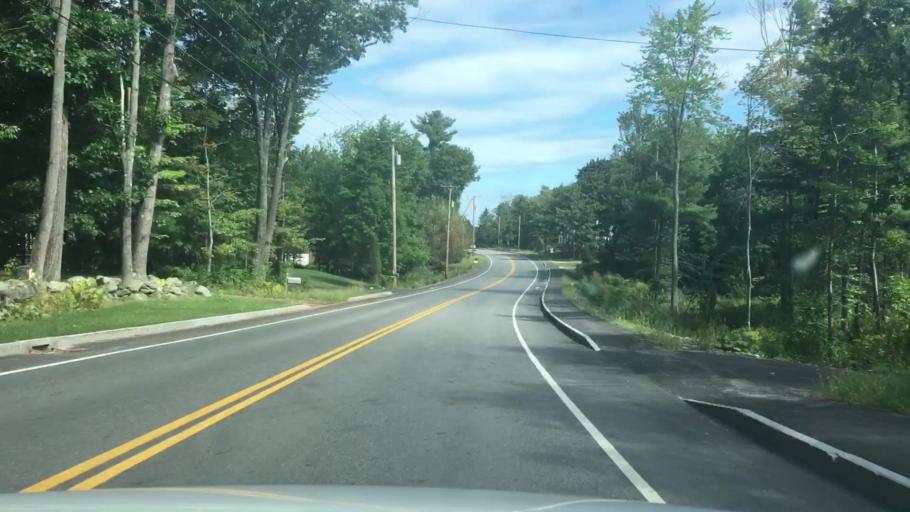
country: US
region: Maine
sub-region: Androscoggin County
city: Auburn
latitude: 44.1155
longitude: -70.2505
